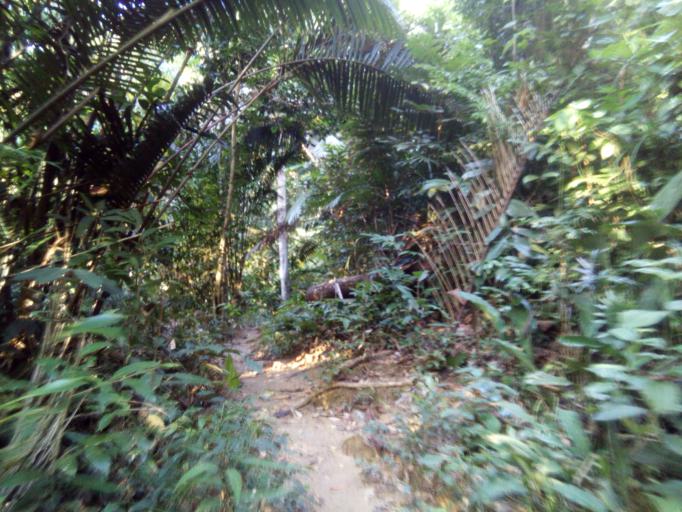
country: MY
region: Penang
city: Tanjung Tokong
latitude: 5.4347
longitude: 100.2899
